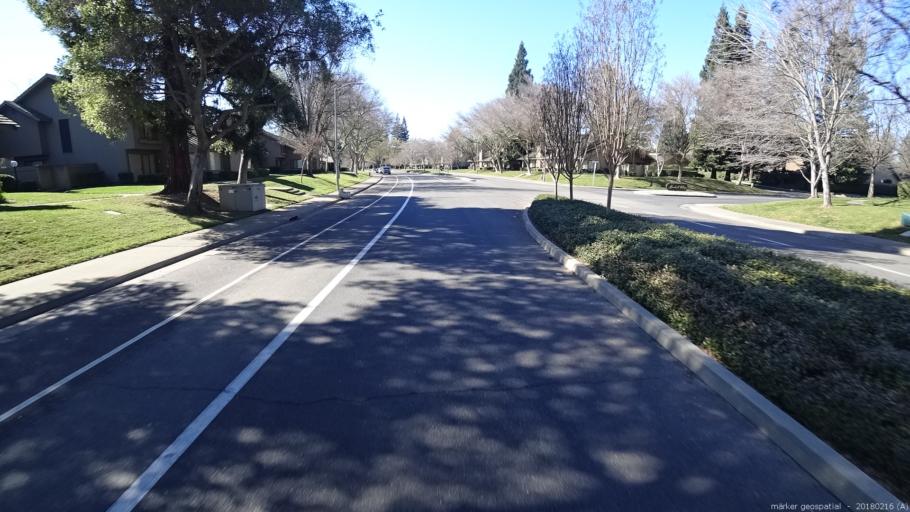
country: US
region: California
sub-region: Sacramento County
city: Gold River
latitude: 38.6324
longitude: -121.2583
